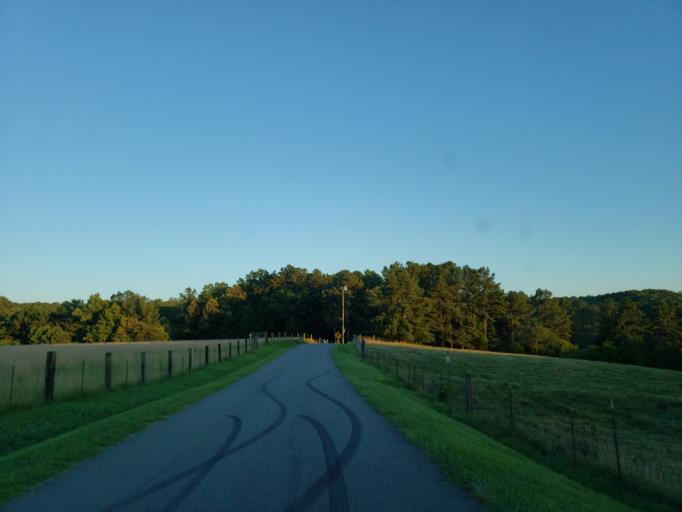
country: US
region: Georgia
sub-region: Bartow County
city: Euharlee
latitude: 34.0986
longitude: -84.8745
